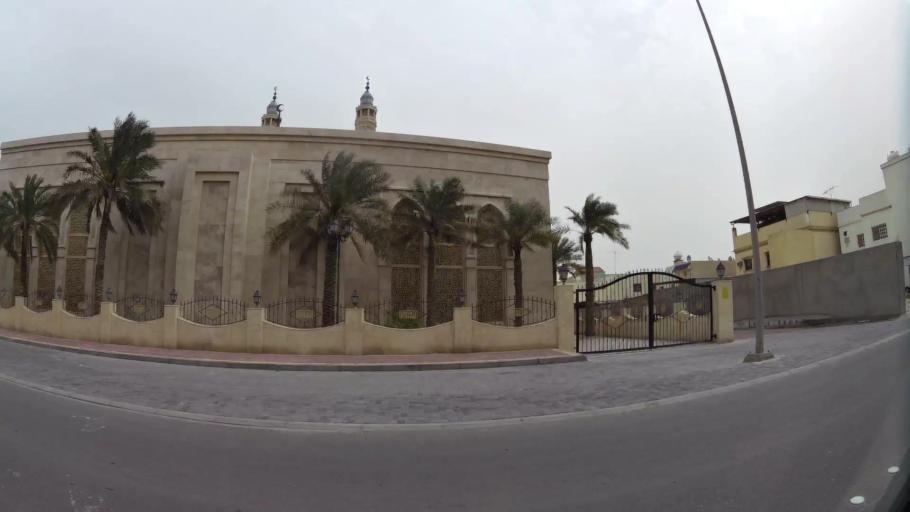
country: BH
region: Northern
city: Madinat `Isa
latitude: 26.1835
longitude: 50.5382
